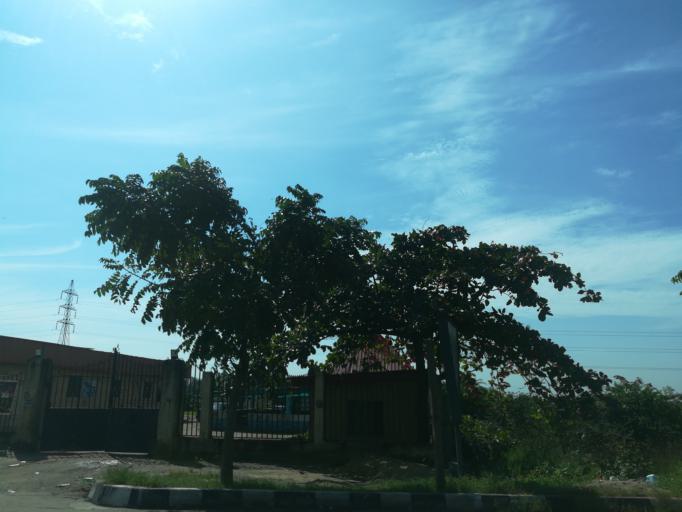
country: NG
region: Lagos
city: Ebute Ikorodu
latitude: 6.6139
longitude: 3.4430
